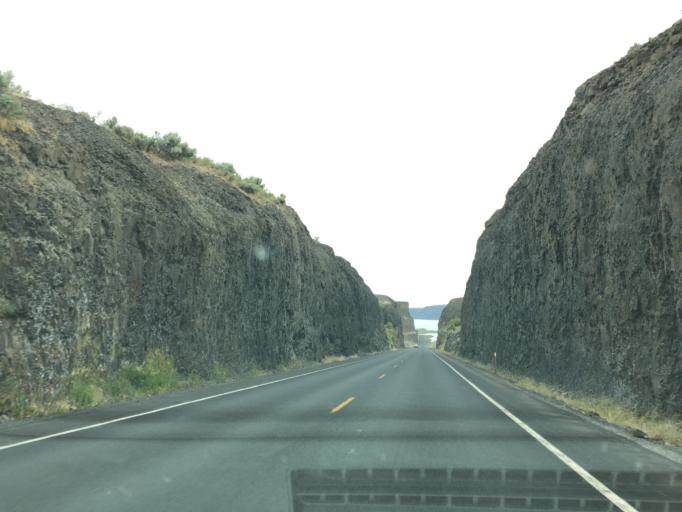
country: US
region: Washington
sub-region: Okanogan County
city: Coulee Dam
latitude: 47.7270
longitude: -119.2502
